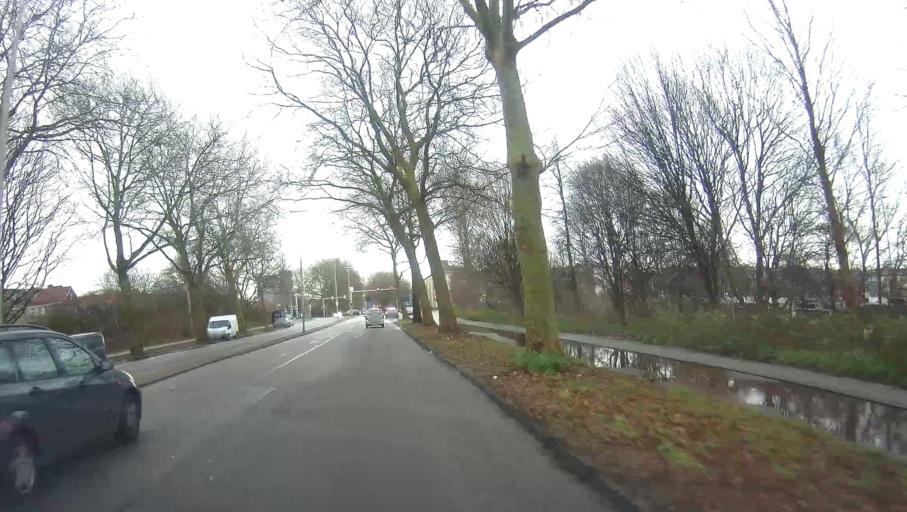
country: NL
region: South Holland
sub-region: Gemeente Den Haag
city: The Hague
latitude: 52.0557
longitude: 4.2951
